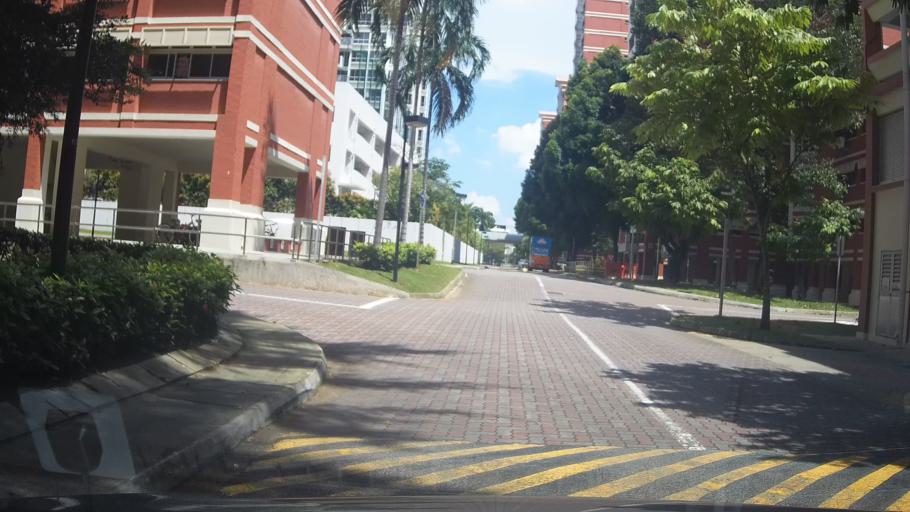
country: MY
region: Johor
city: Kampung Pasir Gudang Baru
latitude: 1.3760
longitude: 103.9419
